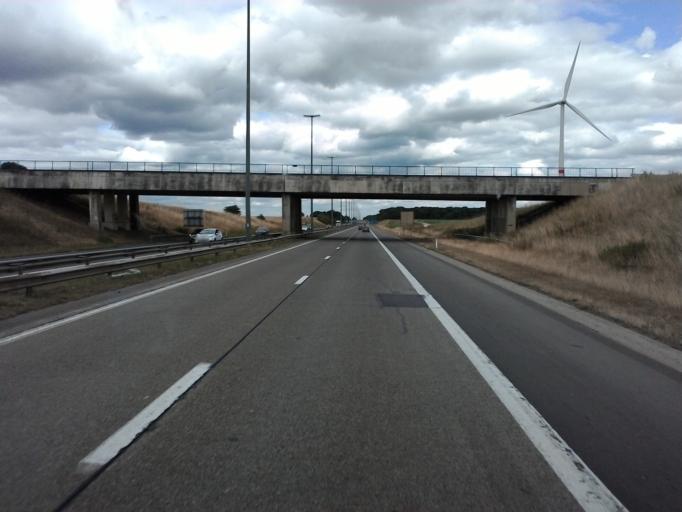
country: LU
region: Luxembourg
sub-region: Canton de Capellen
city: Clemency
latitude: 49.6384
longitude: 5.8650
